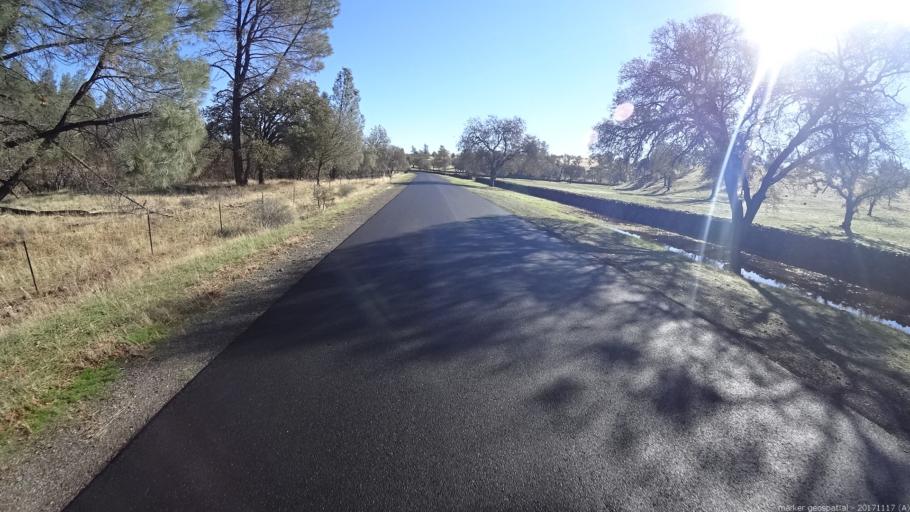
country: US
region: California
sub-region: Shasta County
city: Cottonwood
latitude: 40.4408
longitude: -122.1512
